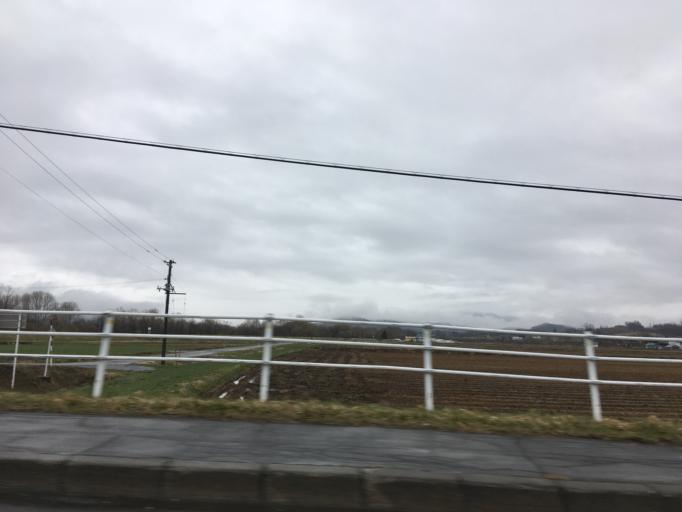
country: JP
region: Hokkaido
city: Nayoro
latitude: 44.1260
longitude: 142.4838
